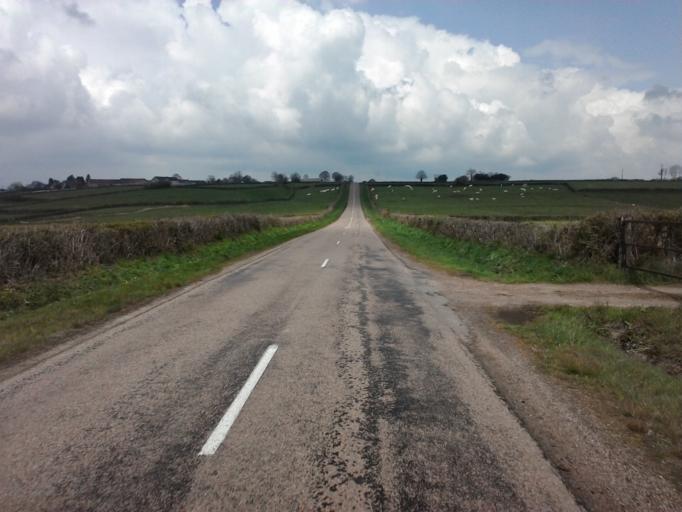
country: FR
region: Bourgogne
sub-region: Departement de la Cote-d'Or
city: Saulieu
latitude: 47.2585
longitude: 4.2250
